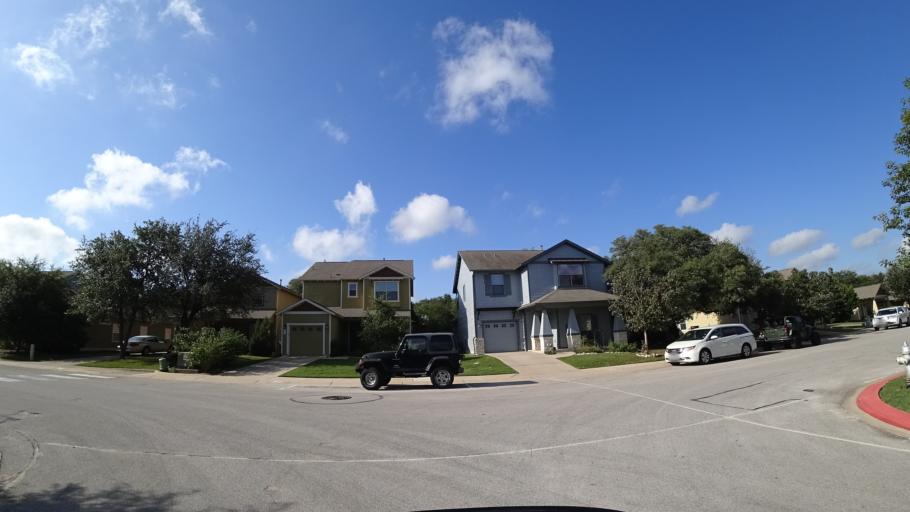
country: US
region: Texas
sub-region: Travis County
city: Rollingwood
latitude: 30.2138
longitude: -97.8061
